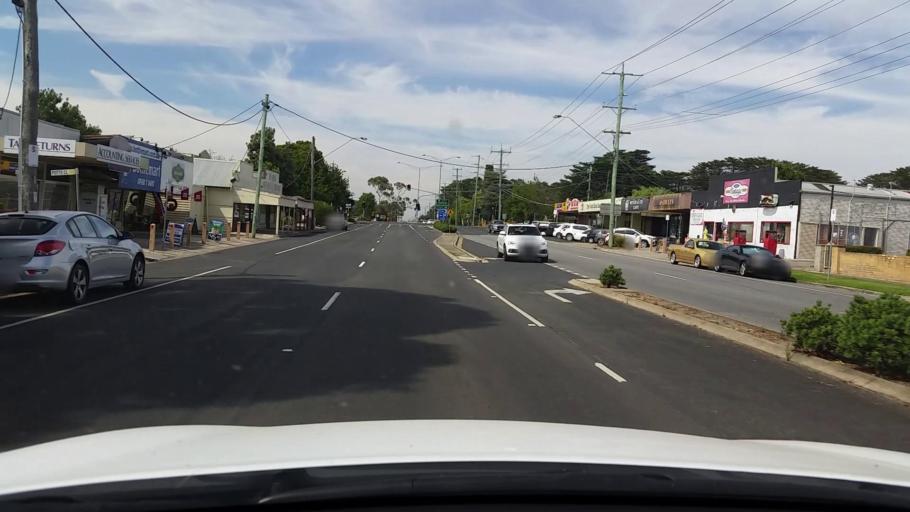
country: AU
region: Victoria
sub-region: Mornington Peninsula
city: Tyabb
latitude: -38.2600
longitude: 145.1898
